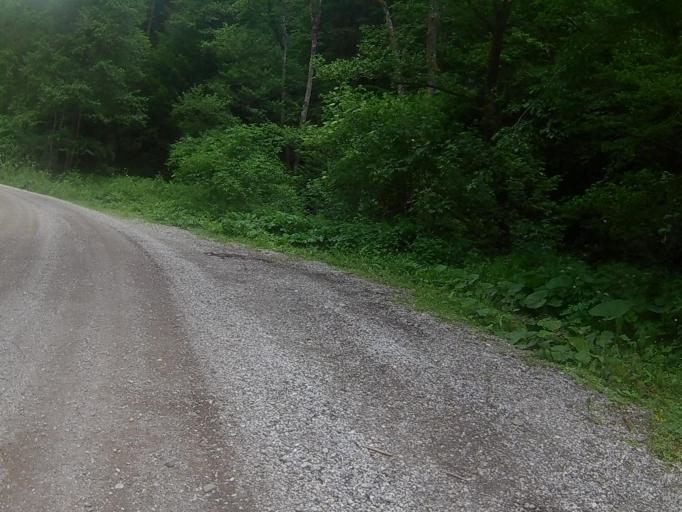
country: SI
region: Maribor
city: Bresternica
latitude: 46.6124
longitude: 15.5712
